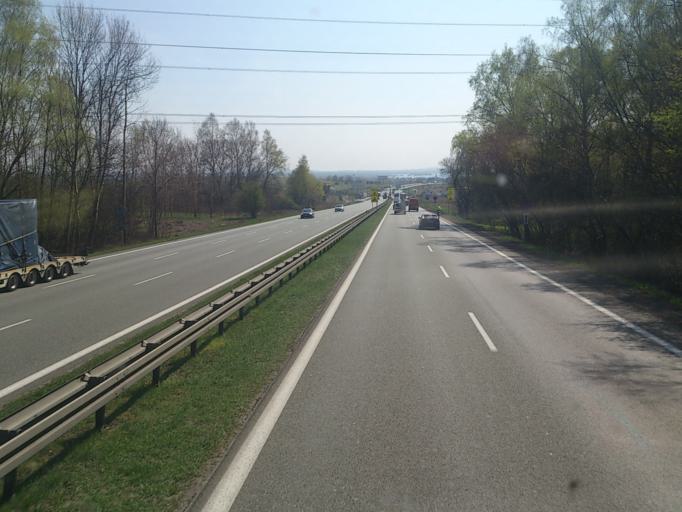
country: PL
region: Silesian Voivodeship
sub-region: Powiat bedzinski
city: Siewierz
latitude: 50.4335
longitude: 19.2148
